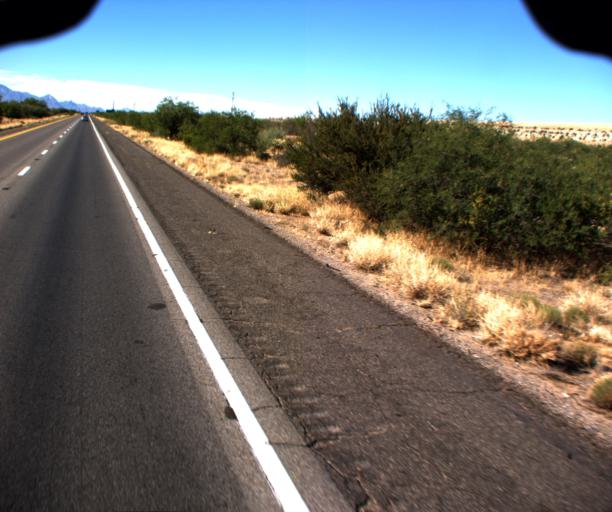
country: US
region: Arizona
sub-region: Pima County
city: Sahuarita
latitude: 31.9806
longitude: -110.9910
